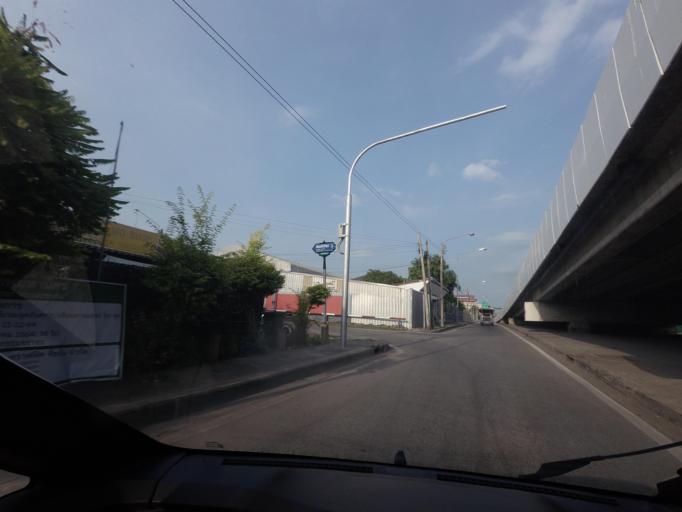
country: TH
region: Bangkok
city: Nong Chok
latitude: 13.8545
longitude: 100.8668
